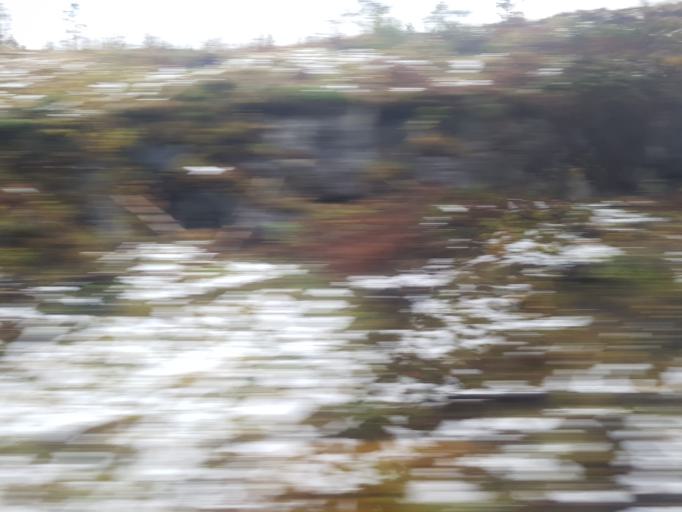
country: NO
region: Sor-Trondelag
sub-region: Rennebu
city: Berkak
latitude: 62.8347
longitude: 10.0123
